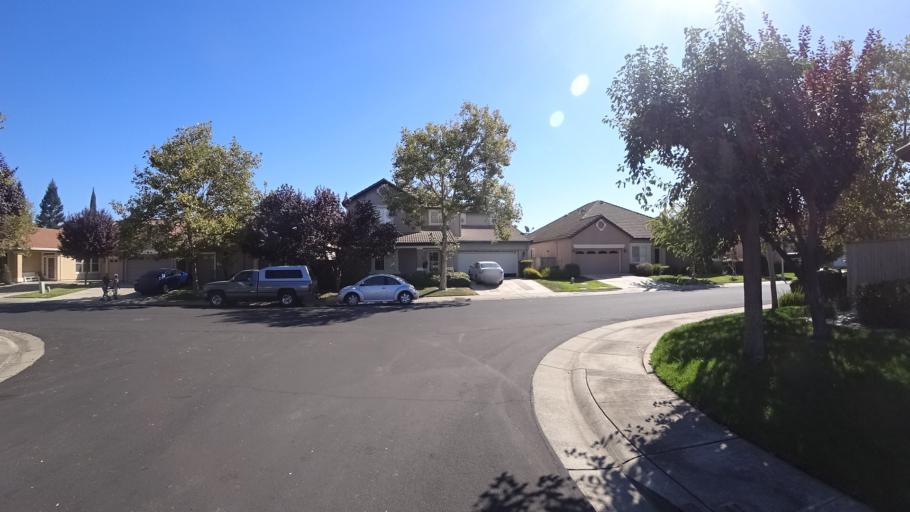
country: US
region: California
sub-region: Sacramento County
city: Laguna
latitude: 38.4179
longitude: -121.4762
